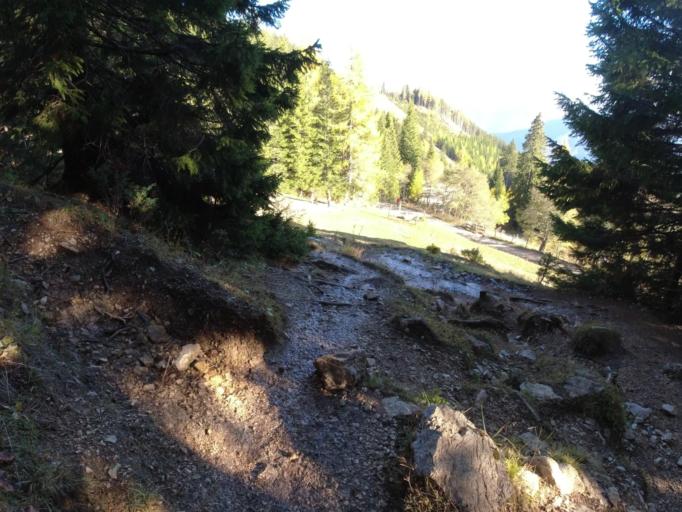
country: AT
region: Carinthia
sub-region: Politischer Bezirk Volkermarkt
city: Gallizien
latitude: 46.5022
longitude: 14.5103
